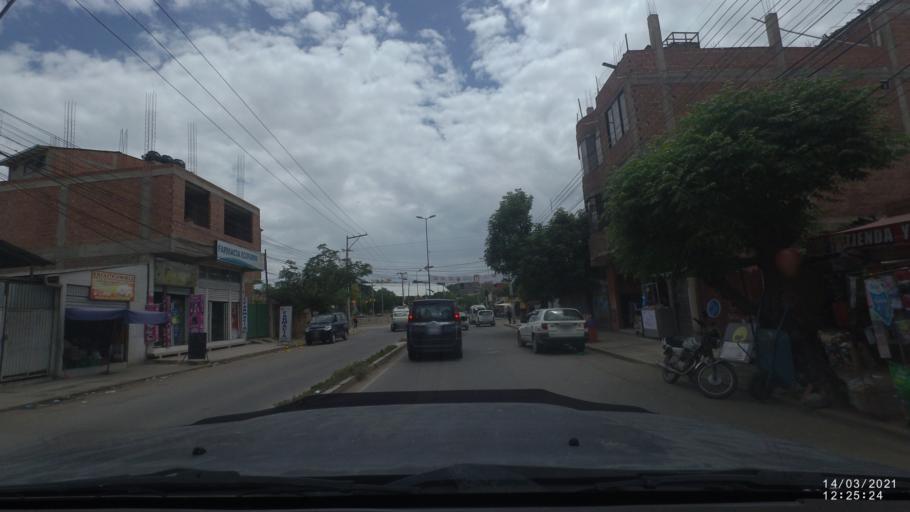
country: BO
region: Cochabamba
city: Cochabamba
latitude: -17.4201
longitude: -66.1389
